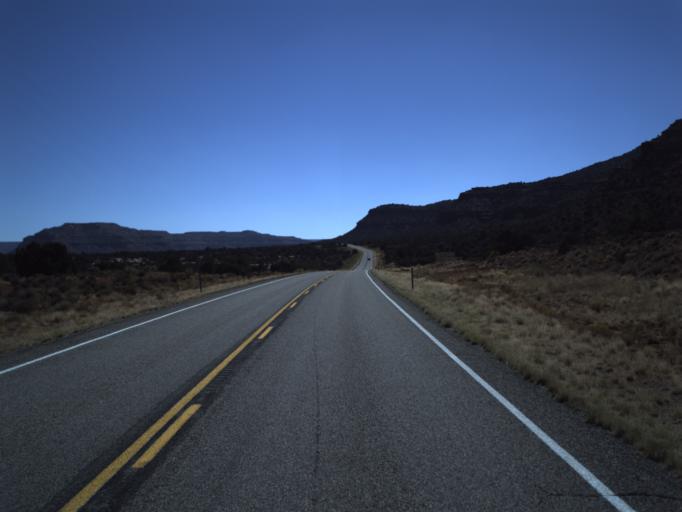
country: US
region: Utah
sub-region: San Juan County
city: Blanding
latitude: 37.6724
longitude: -110.2040
